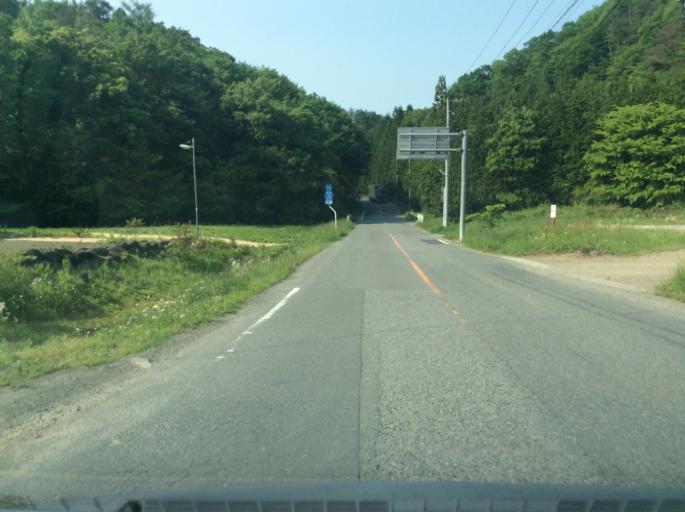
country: JP
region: Tochigi
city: Kuroiso
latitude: 37.0814
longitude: 140.2241
